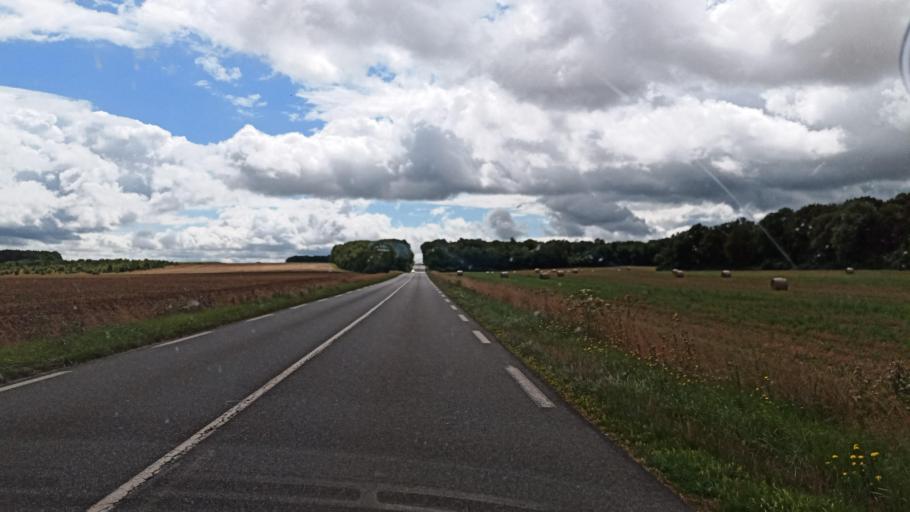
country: FR
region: Ile-de-France
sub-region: Departement de Seine-et-Marne
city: Montereau-Fault-Yonne
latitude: 48.3543
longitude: 2.9572
